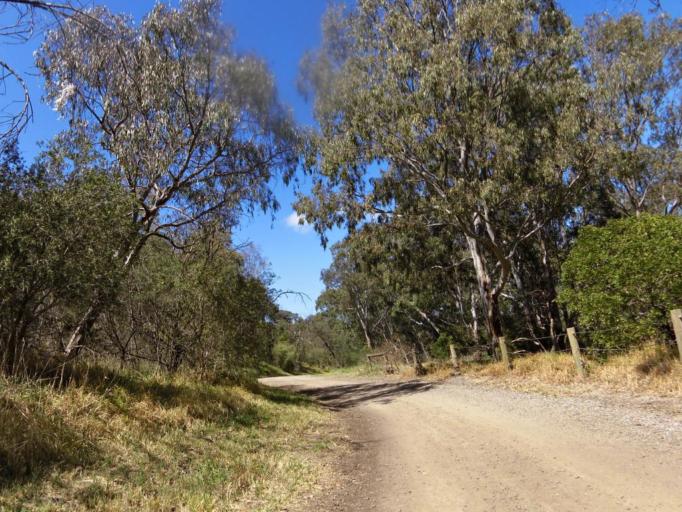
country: AU
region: Victoria
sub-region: Brimbank
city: Albion
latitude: -37.7522
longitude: 144.8490
